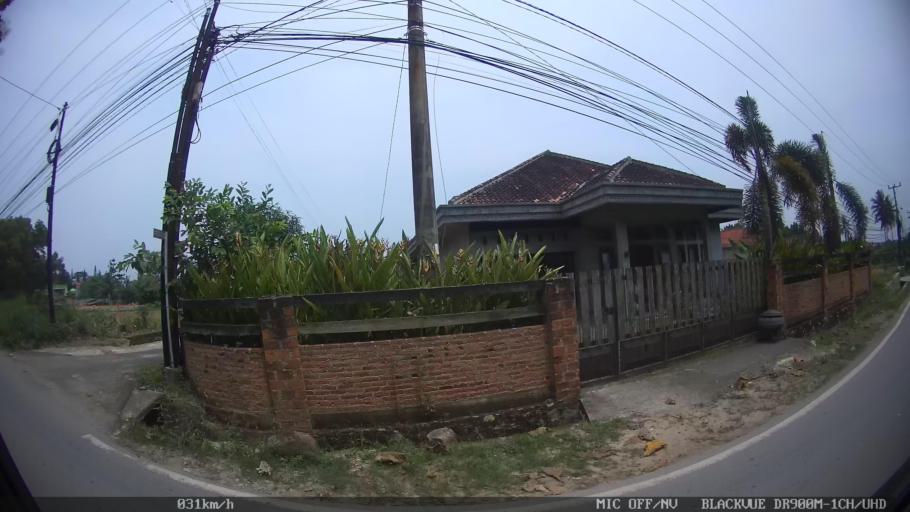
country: ID
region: Lampung
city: Kedaton
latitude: -5.4013
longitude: 105.3168
